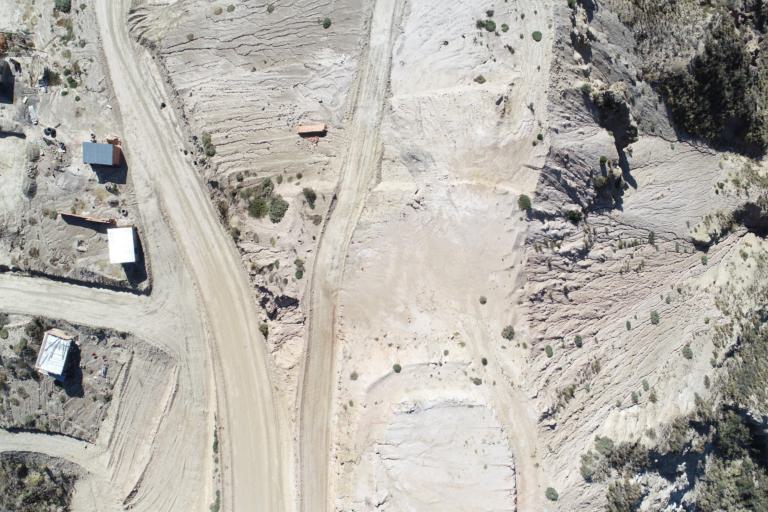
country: BO
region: La Paz
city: La Paz
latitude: -16.5492
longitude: -68.1077
